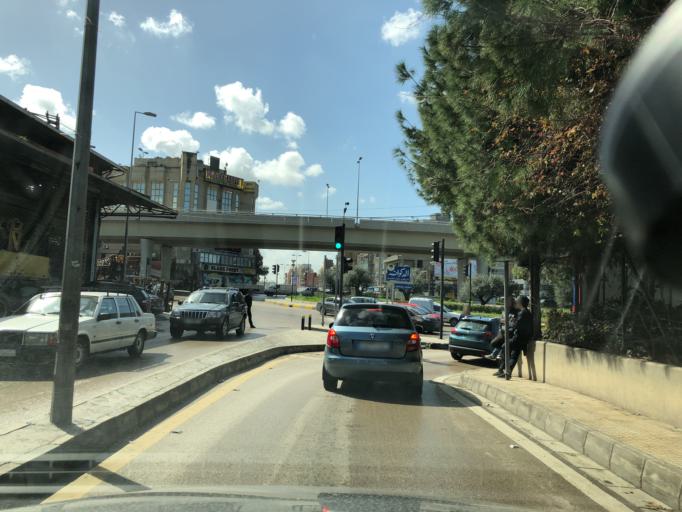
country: LB
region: Mont-Liban
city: Jdaidet el Matn
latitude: 33.8697
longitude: 35.5431
